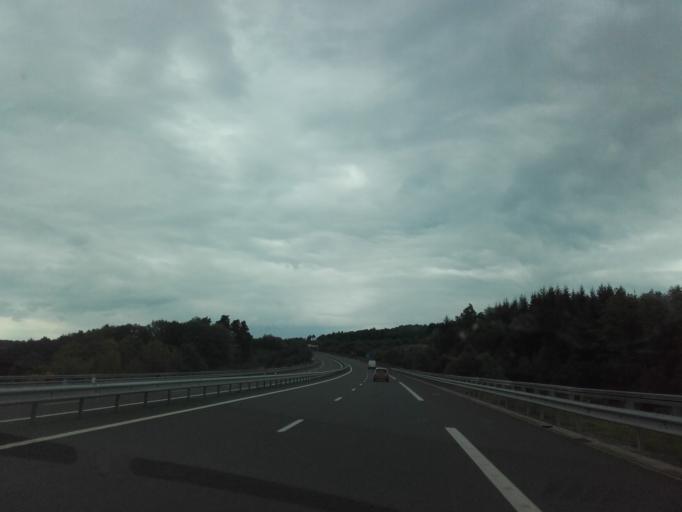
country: FR
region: Limousin
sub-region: Departement de la Correze
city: Ussel
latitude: 45.5563
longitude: 2.3702
